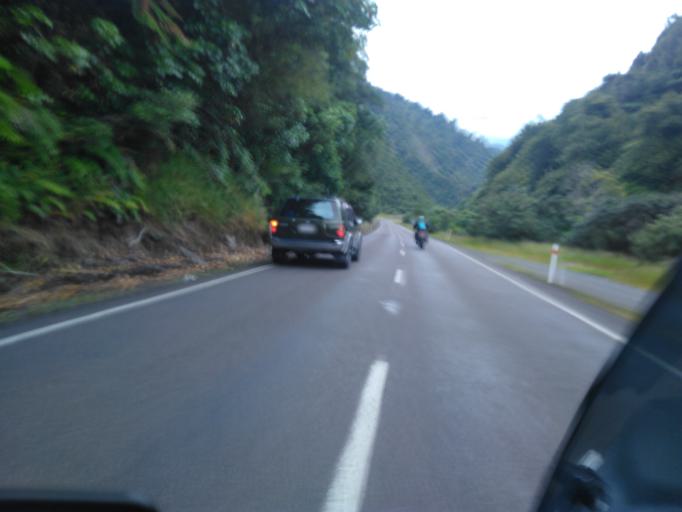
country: NZ
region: Bay of Plenty
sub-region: Opotiki District
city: Opotiki
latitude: -38.3144
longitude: 177.3962
